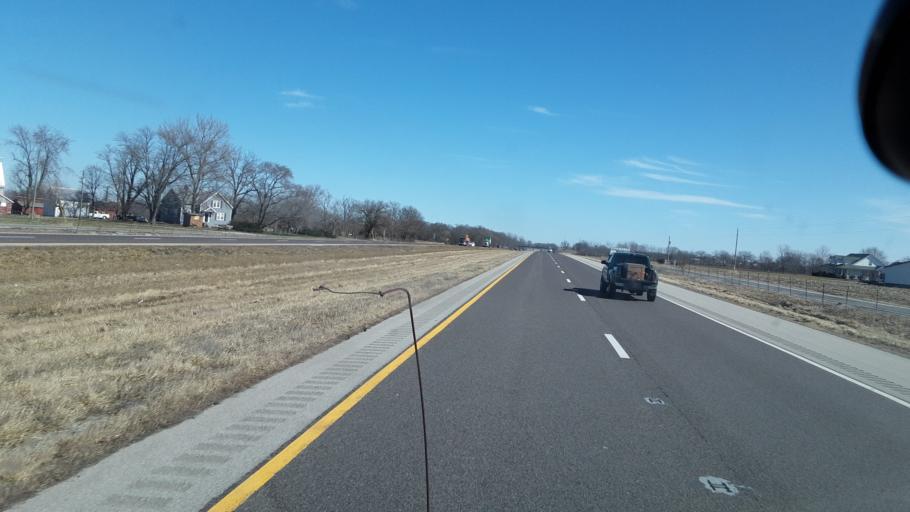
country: US
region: Illinois
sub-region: Madison County
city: Highland
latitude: 38.7961
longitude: -89.6085
